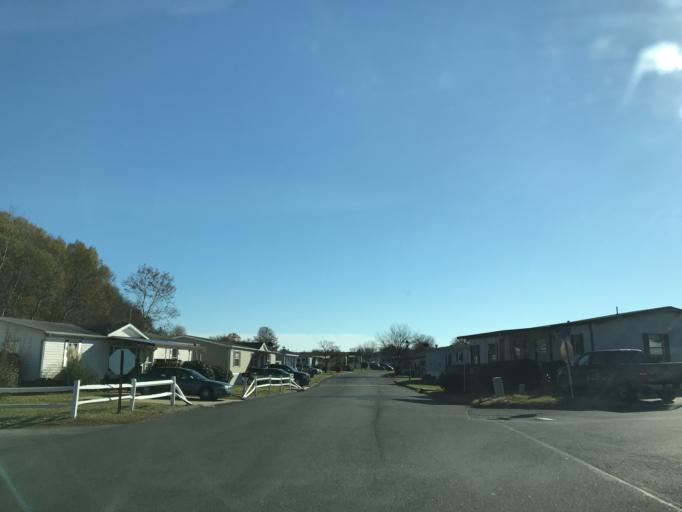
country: US
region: Maryland
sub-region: Baltimore County
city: Bowleys Quarters
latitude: 39.3469
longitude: -76.3779
